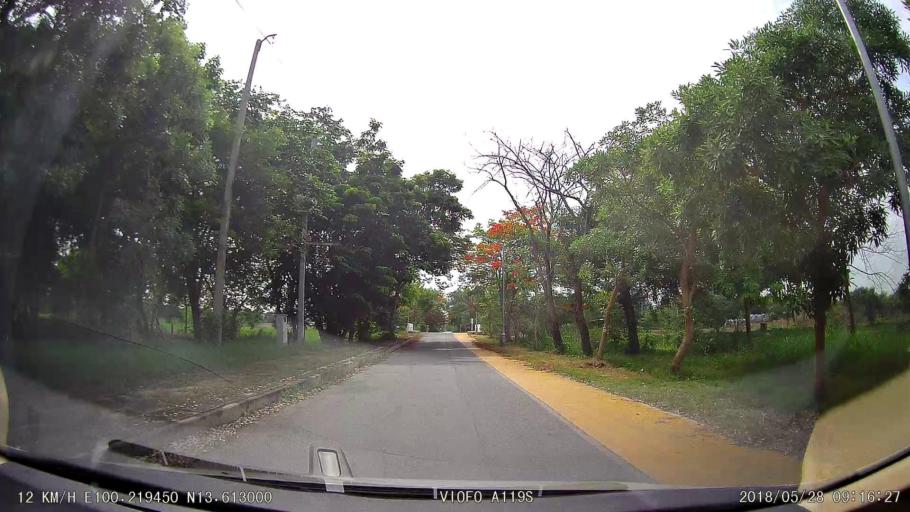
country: TH
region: Samut Sakhon
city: Krathum Baen
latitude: 13.6130
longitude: 100.2223
